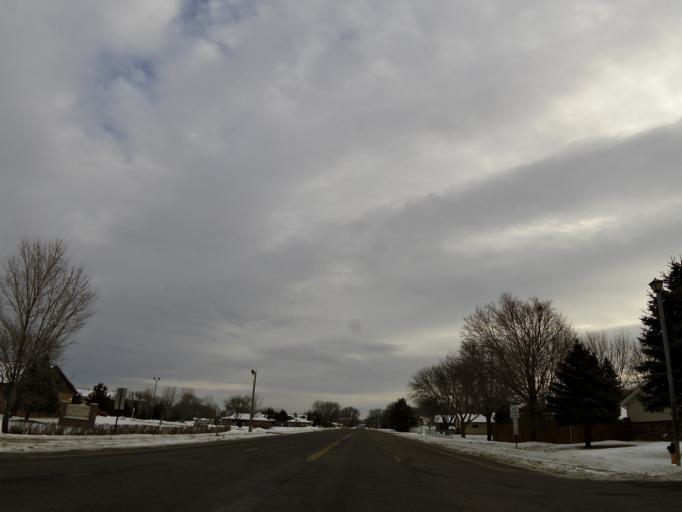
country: US
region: Minnesota
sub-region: Scott County
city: Shakopee
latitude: 44.7883
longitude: -93.5106
